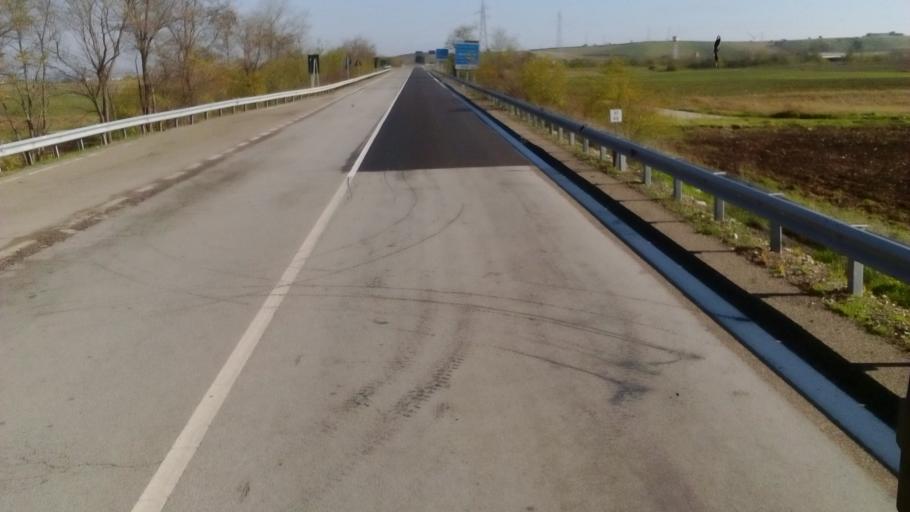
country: IT
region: Basilicate
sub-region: Provincia di Potenza
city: Melfi
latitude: 41.0658
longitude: 15.6704
